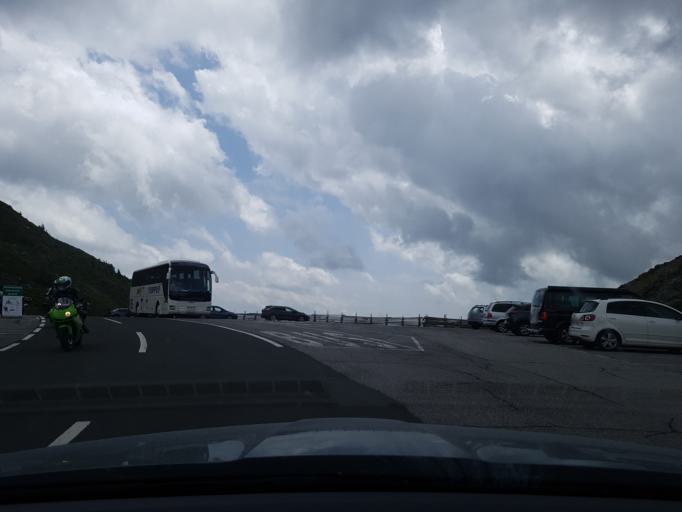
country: AT
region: Carinthia
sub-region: Politischer Bezirk Spittal an der Drau
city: Kleinkirchheim
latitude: 46.8900
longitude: 13.7938
